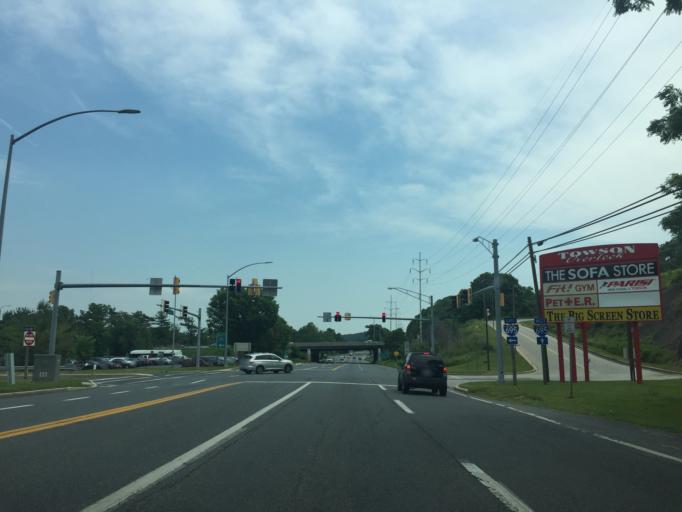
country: US
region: Maryland
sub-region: Baltimore County
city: Hampton
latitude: 39.4010
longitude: -76.5711
